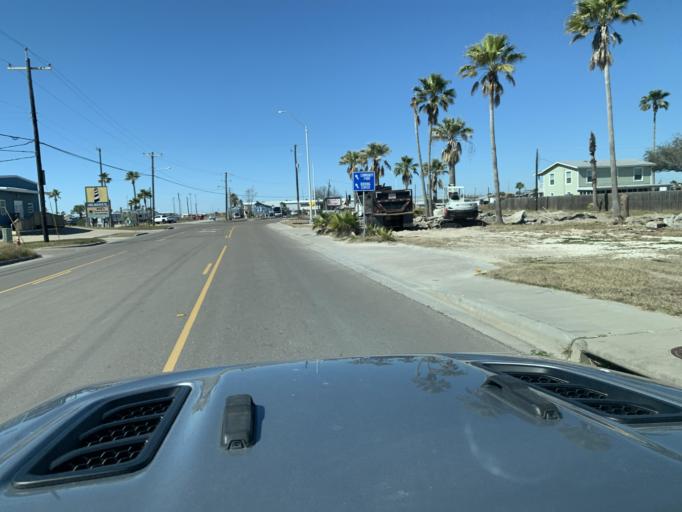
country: US
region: Texas
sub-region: Nueces County
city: Port Aransas
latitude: 27.8305
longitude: -97.0703
